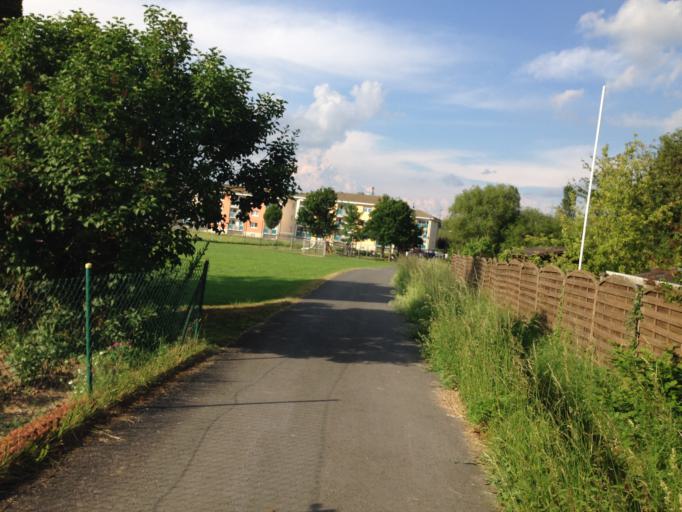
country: DE
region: Hesse
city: Allendorf an der Lahn
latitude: 50.5487
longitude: 8.6193
